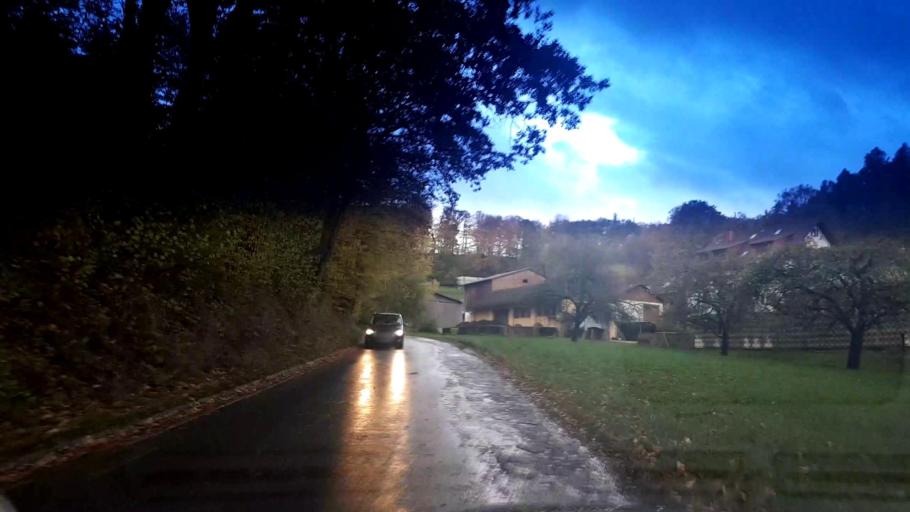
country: DE
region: Bavaria
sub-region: Upper Franconia
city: Viereth-Trunstadt
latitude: 49.9173
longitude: 10.7778
